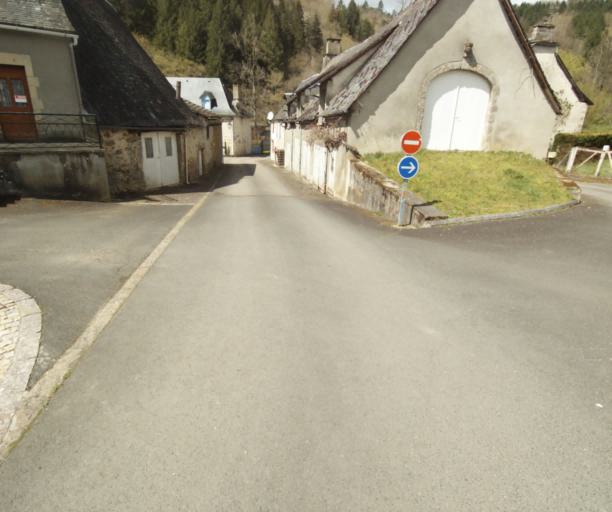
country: FR
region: Limousin
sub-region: Departement de la Correze
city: Argentat
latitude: 45.1760
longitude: 1.8756
